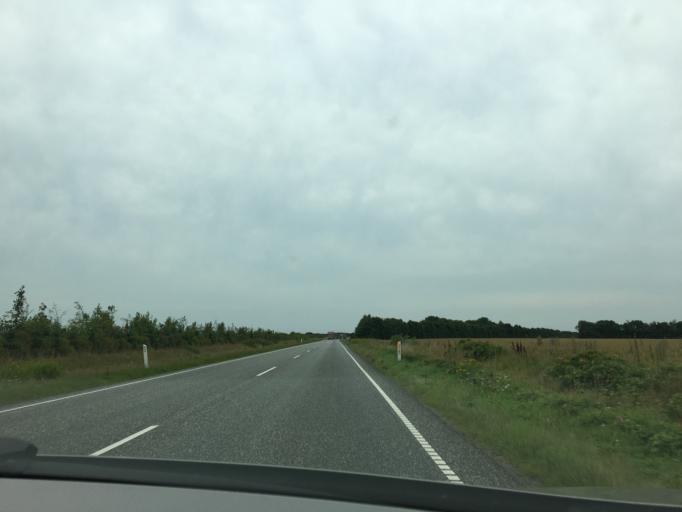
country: DK
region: Central Jutland
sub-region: Herning Kommune
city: Sunds
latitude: 56.2273
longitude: 9.0091
